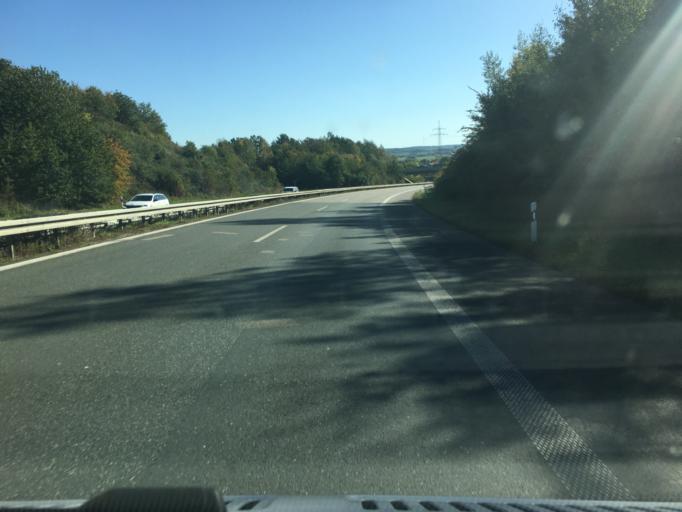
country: DE
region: Saxony
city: Dennheritz
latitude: 50.7903
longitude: 12.4737
